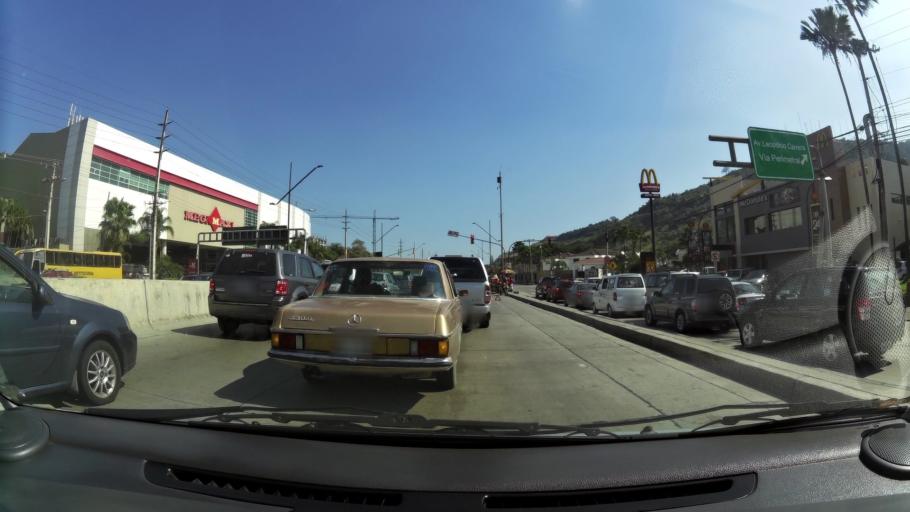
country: EC
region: Guayas
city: Guayaquil
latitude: -2.1725
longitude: -79.9399
